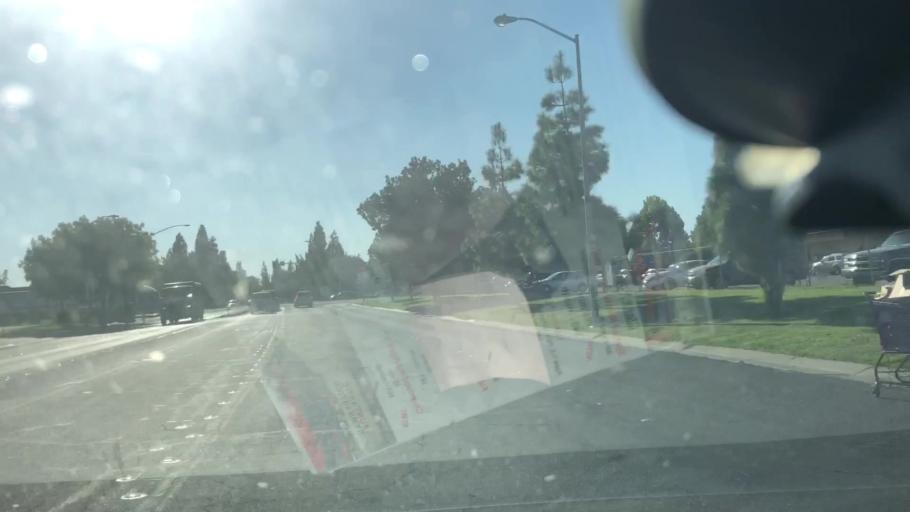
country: US
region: California
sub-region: San Joaquin County
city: Manteca
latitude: 37.7877
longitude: -121.2146
